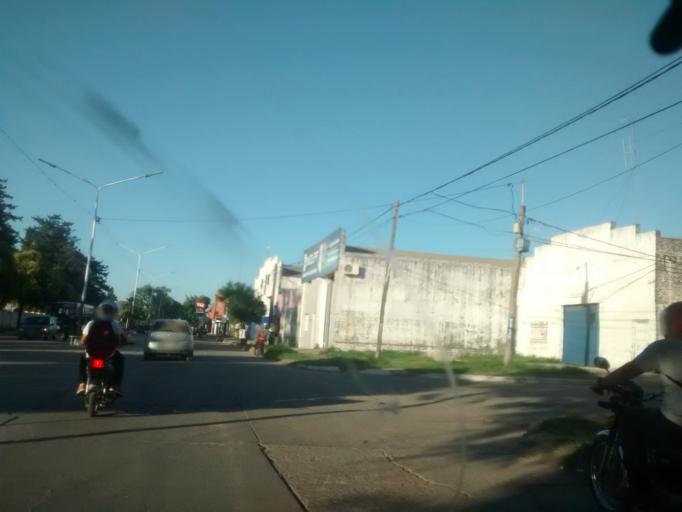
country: AR
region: Chaco
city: Resistencia
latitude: -27.4572
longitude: -59.0074
